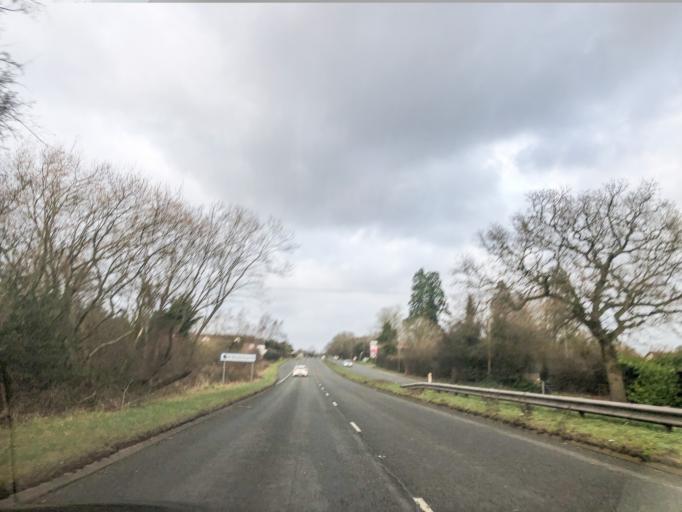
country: GB
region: England
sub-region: Solihull
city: Tidbury Green
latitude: 52.3662
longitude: -1.8885
